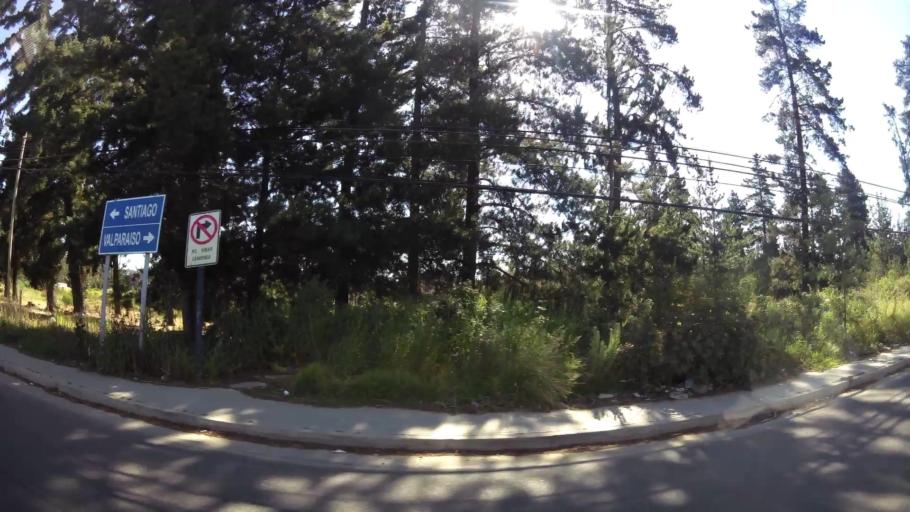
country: CL
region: Valparaiso
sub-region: Provincia de Valparaiso
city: Vina del Mar
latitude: -33.1329
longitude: -71.5648
